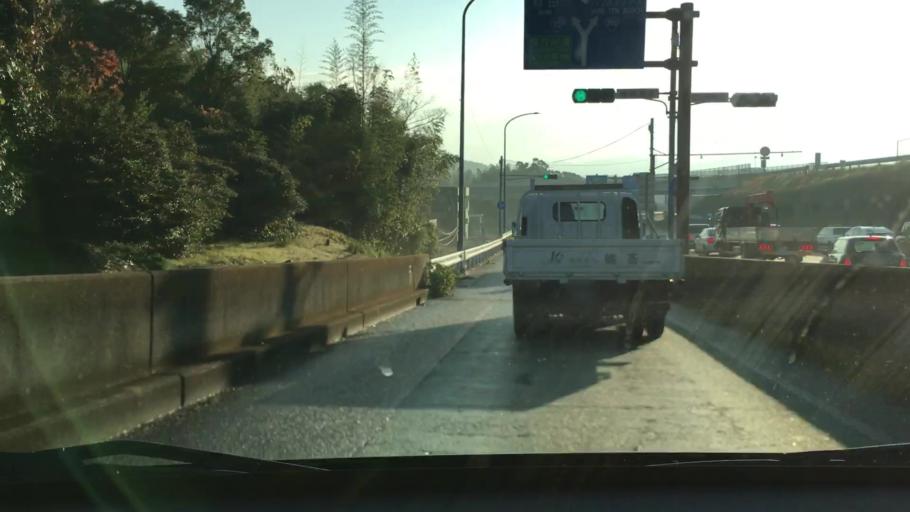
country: JP
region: Nagasaki
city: Sasebo
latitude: 33.1475
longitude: 129.7753
